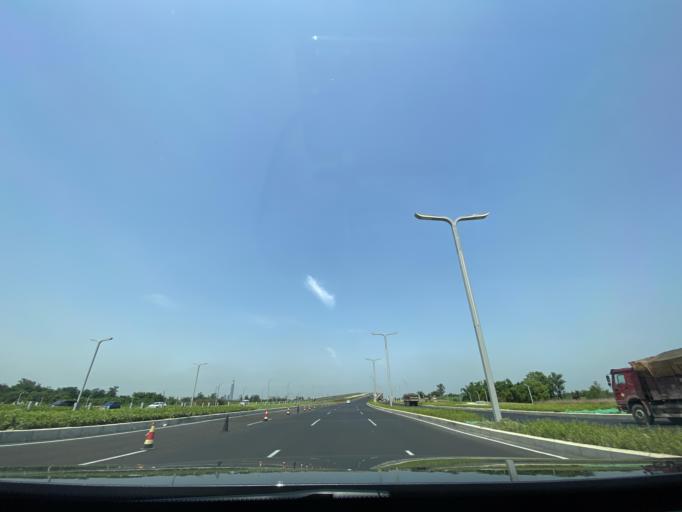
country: CN
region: Sichuan
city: Longquan
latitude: 30.6144
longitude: 104.2199
